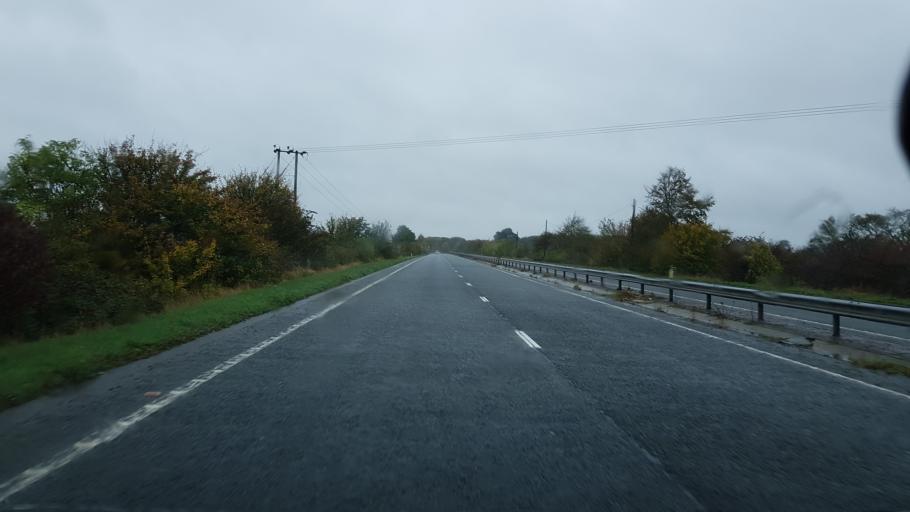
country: GB
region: England
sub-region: Oxfordshire
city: Carterton
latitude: 51.7866
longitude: -1.5736
